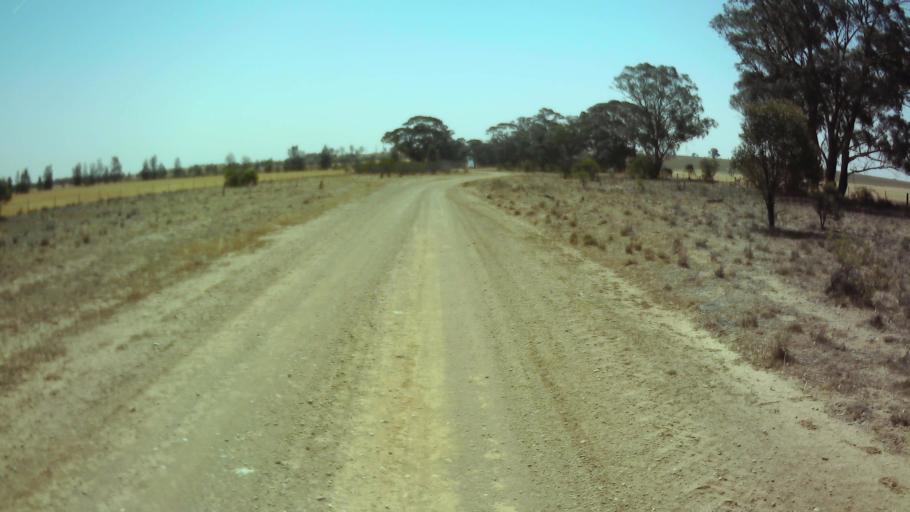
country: AU
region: New South Wales
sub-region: Weddin
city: Grenfell
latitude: -33.9123
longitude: 147.7693
